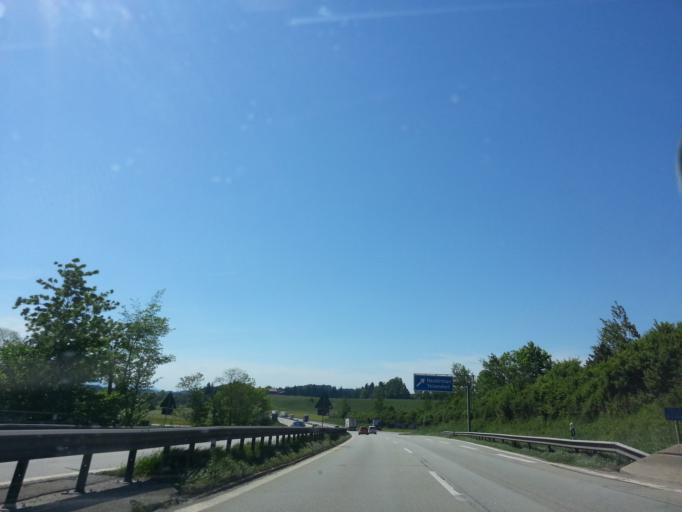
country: DE
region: Bavaria
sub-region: Upper Bavaria
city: Surberg
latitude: 47.8309
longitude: 12.7426
